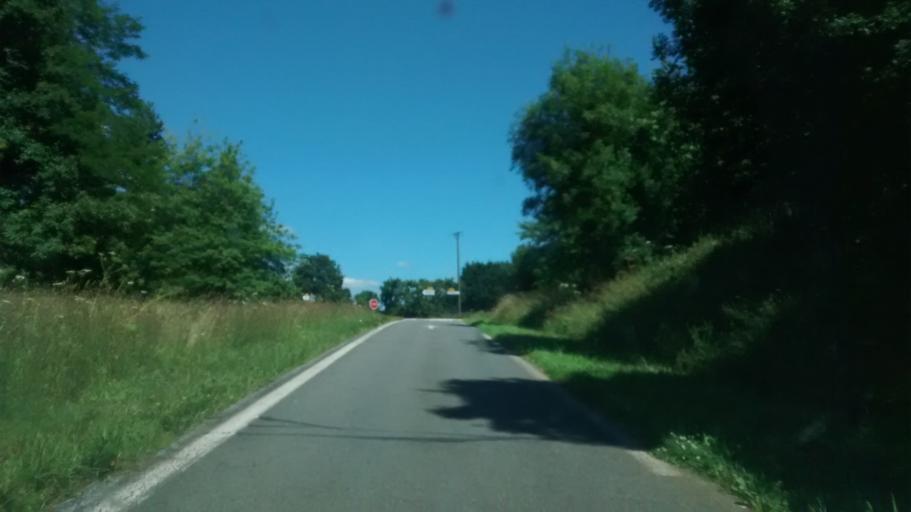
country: FR
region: Brittany
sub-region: Departement des Cotes-d'Armor
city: Louargat
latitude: 48.5616
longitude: -3.3363
